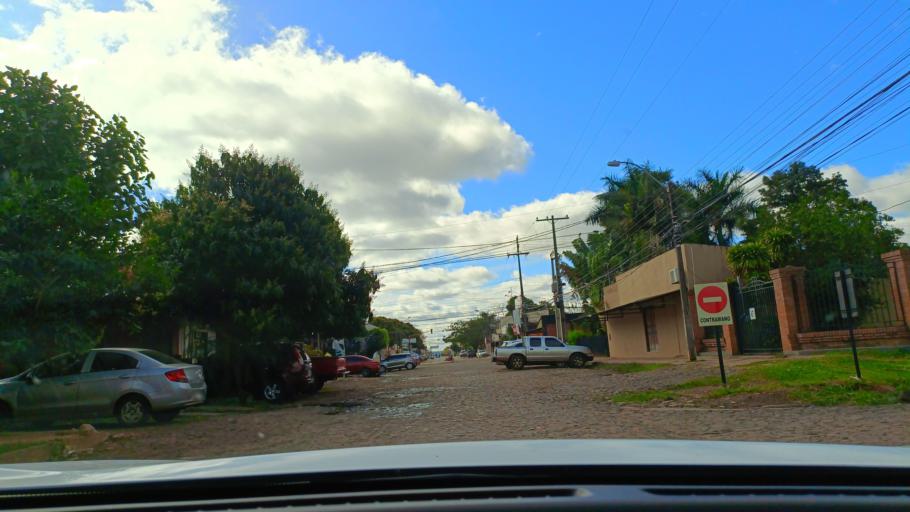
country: PY
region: San Pedro
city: Guayaybi
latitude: -24.6758
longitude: -56.4470
